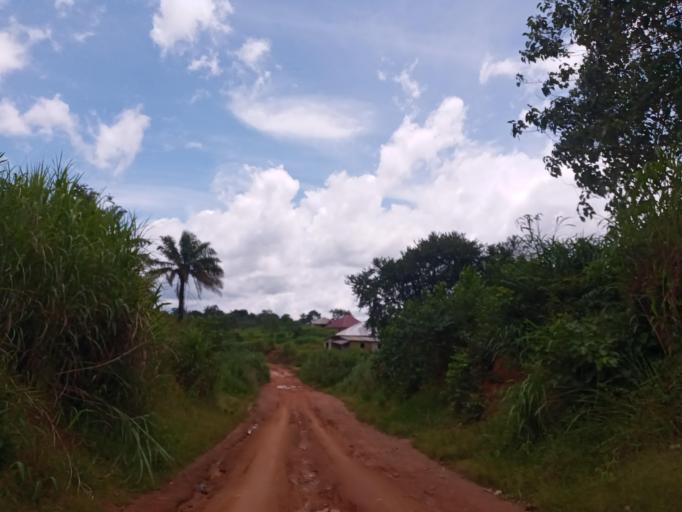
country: SL
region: Eastern Province
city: Koidu
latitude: 8.6449
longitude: -10.9217
